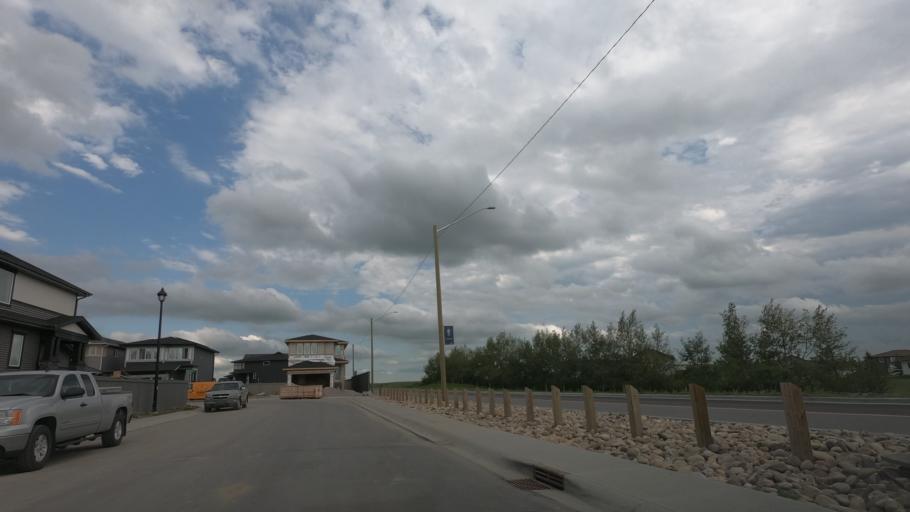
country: CA
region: Alberta
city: Airdrie
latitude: 51.2565
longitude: -113.9874
